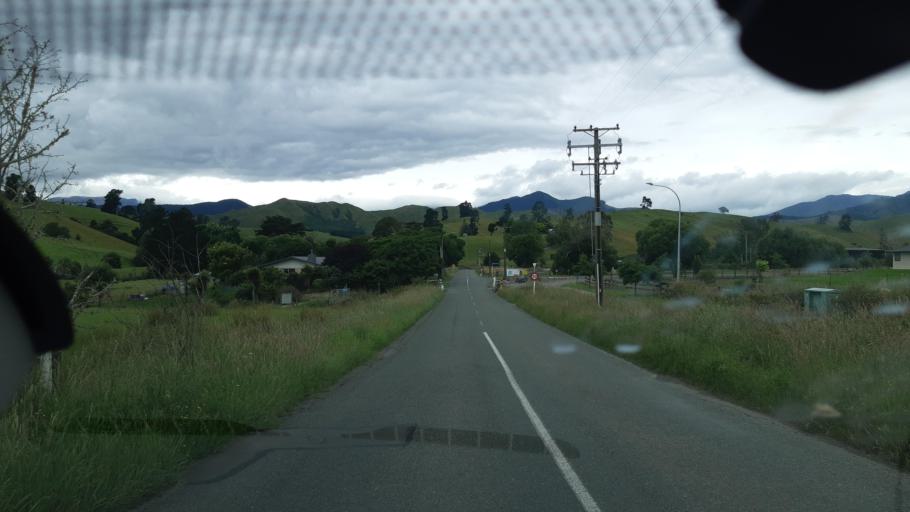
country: NZ
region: Tasman
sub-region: Tasman District
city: Wakefield
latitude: -41.4117
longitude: 173.0497
